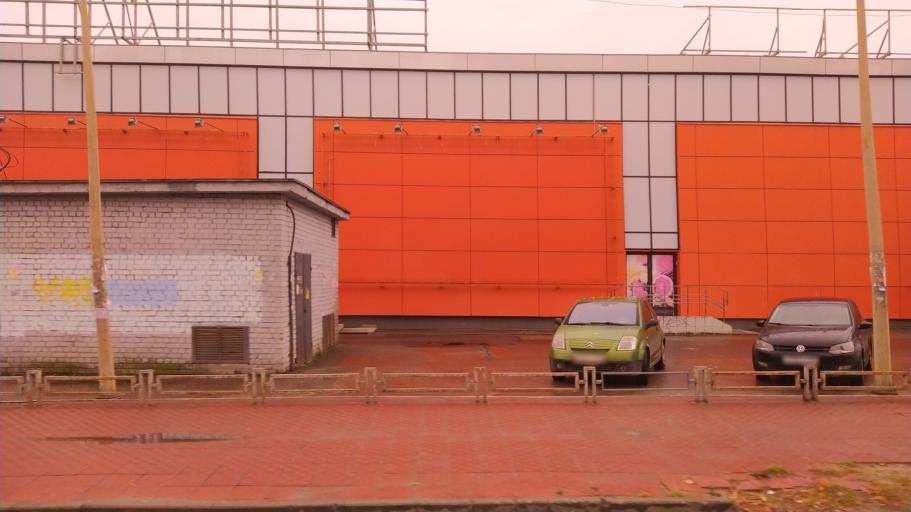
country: RU
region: Tverskaya
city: Tver
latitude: 56.8350
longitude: 35.8977
